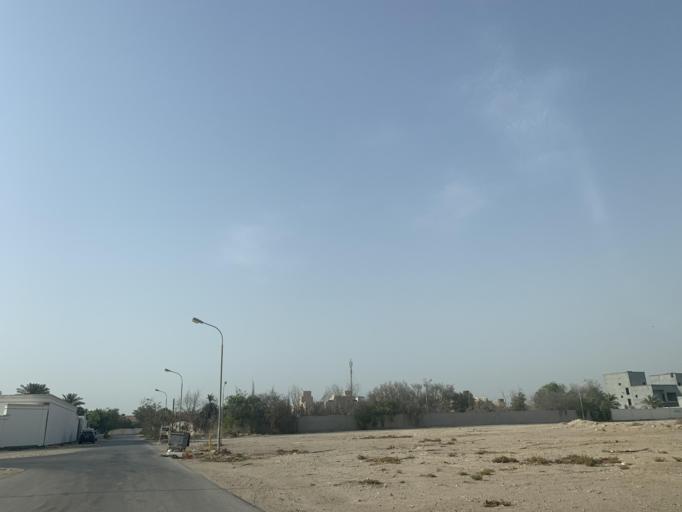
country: BH
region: Central Governorate
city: Madinat Hamad
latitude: 26.1763
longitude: 50.4713
